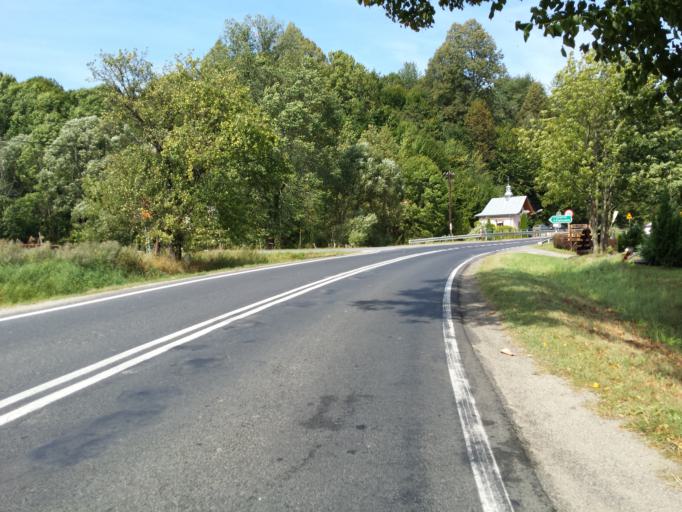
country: PL
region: Subcarpathian Voivodeship
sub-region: Powiat leski
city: Baligrod
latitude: 49.3611
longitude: 22.2770
